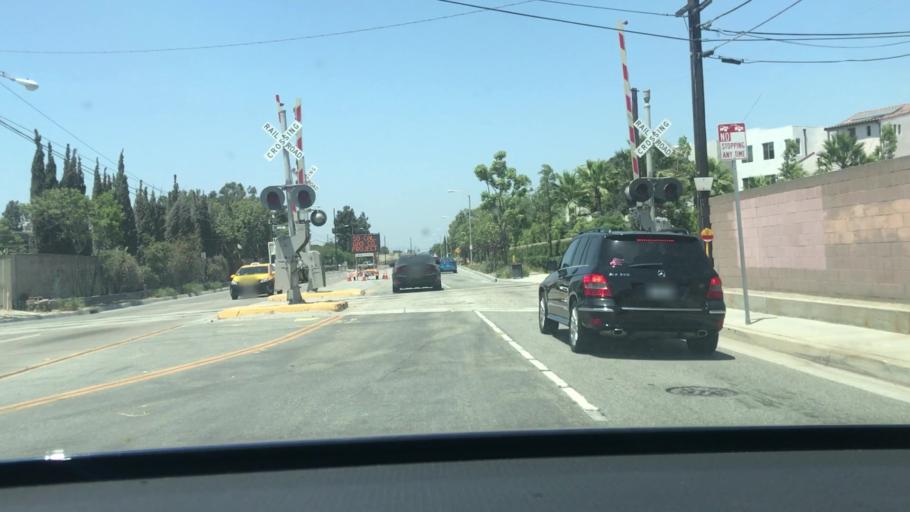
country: US
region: California
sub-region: Los Angeles County
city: Del Aire
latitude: 33.9119
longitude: -118.3787
